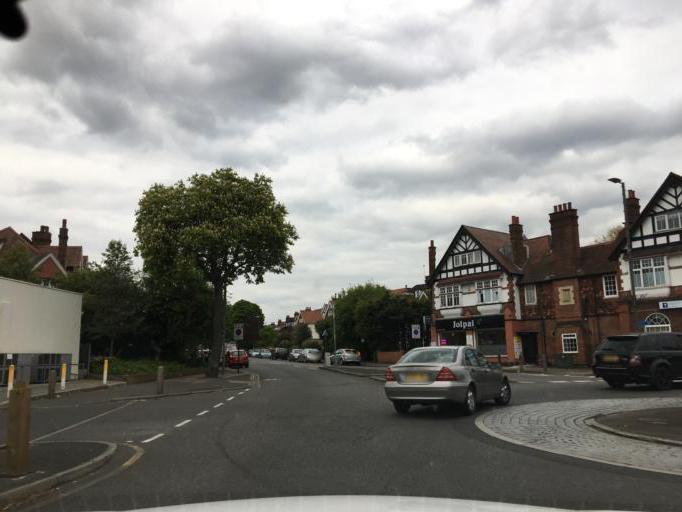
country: GB
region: England
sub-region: Greater London
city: Chislehurst
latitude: 51.4376
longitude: 0.0429
